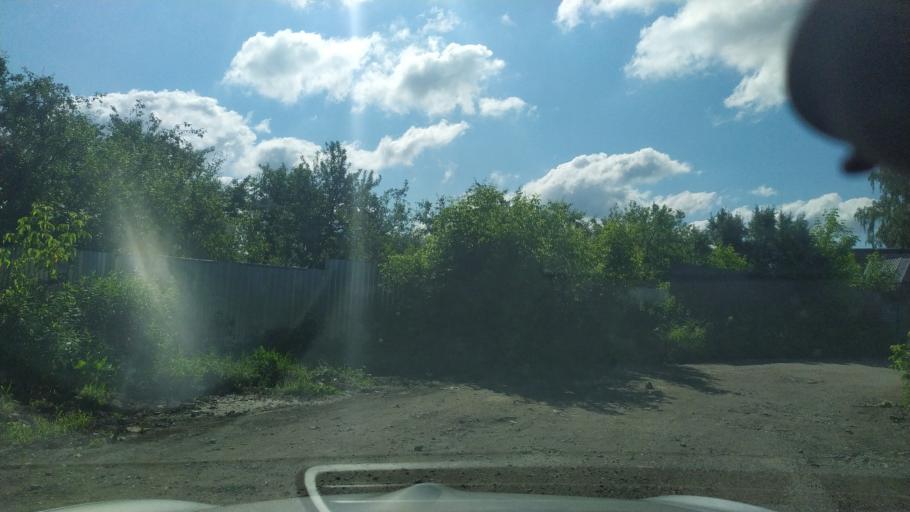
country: RU
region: Moscow
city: Vostochnyy
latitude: 55.8137
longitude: 37.8659
